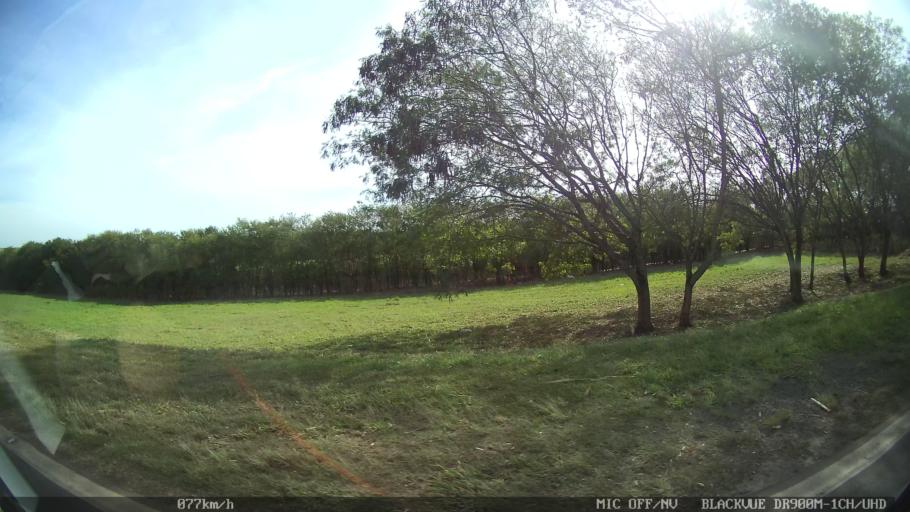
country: BR
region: Sao Paulo
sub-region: Rio Das Pedras
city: Rio das Pedras
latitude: -22.7953
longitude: -47.5920
